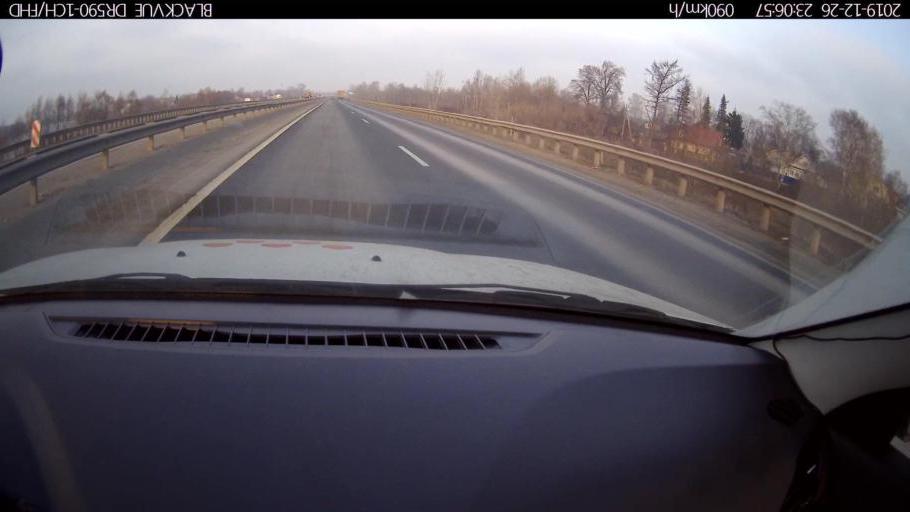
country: RU
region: Nizjnij Novgorod
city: Gorbatovka
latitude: 56.2123
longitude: 43.7514
